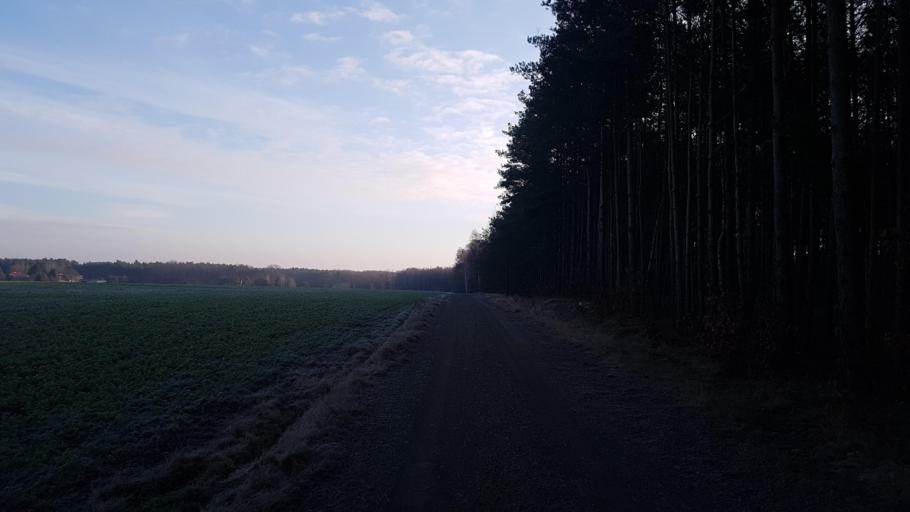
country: DE
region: Brandenburg
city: Plessa
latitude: 51.5288
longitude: 13.6720
